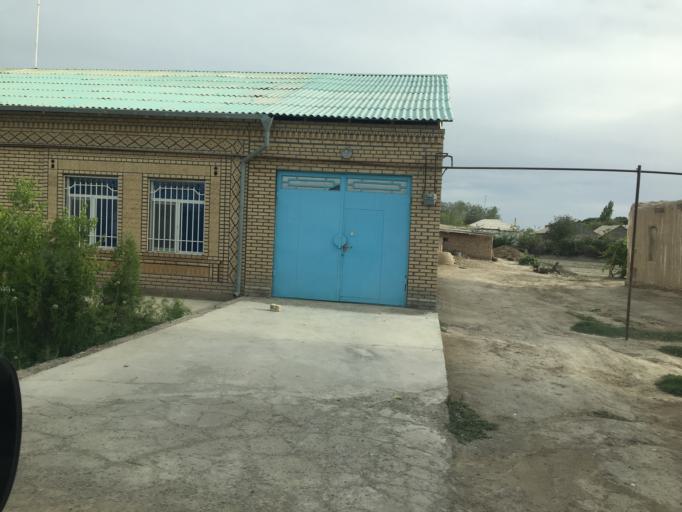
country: TM
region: Dasoguz
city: Dasoguz
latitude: 41.8202
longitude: 59.9189
